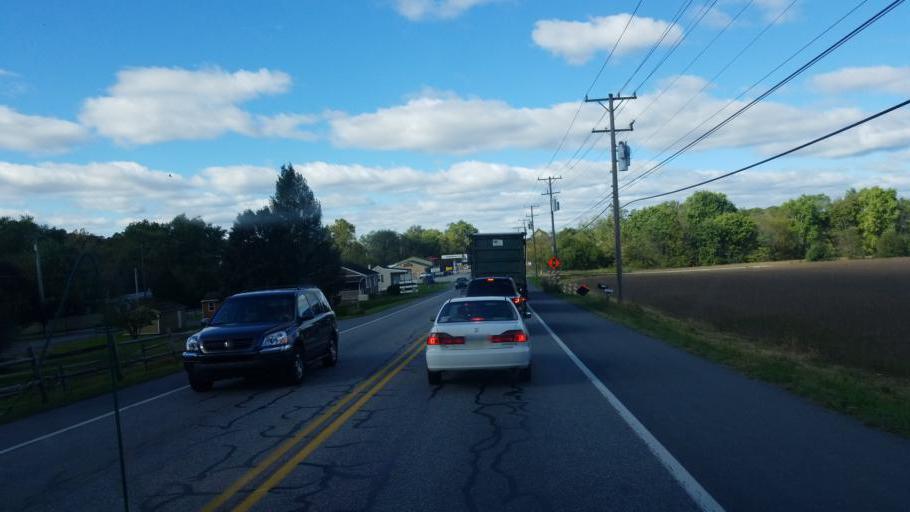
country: US
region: Pennsylvania
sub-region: Franklin County
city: Greencastle
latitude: 39.7922
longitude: -77.7501
